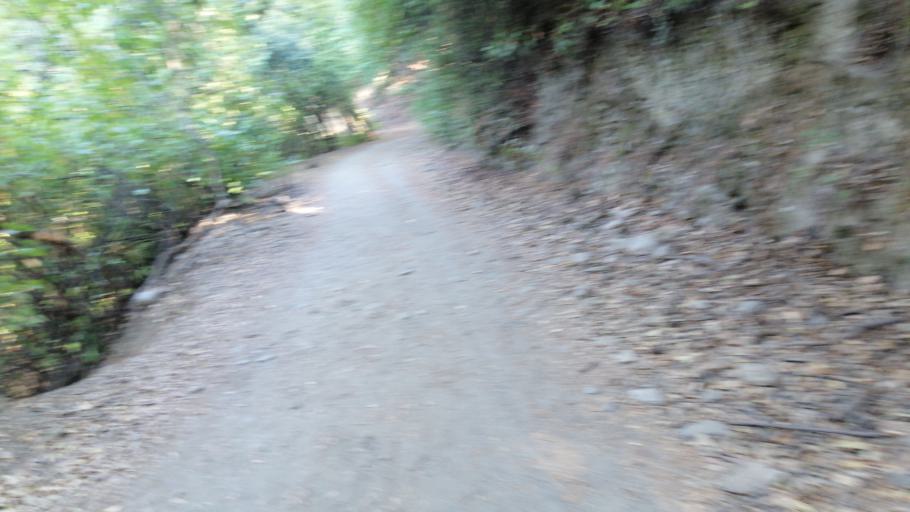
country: TR
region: Aydin
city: Atburgazi
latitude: 37.6902
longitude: 27.1346
